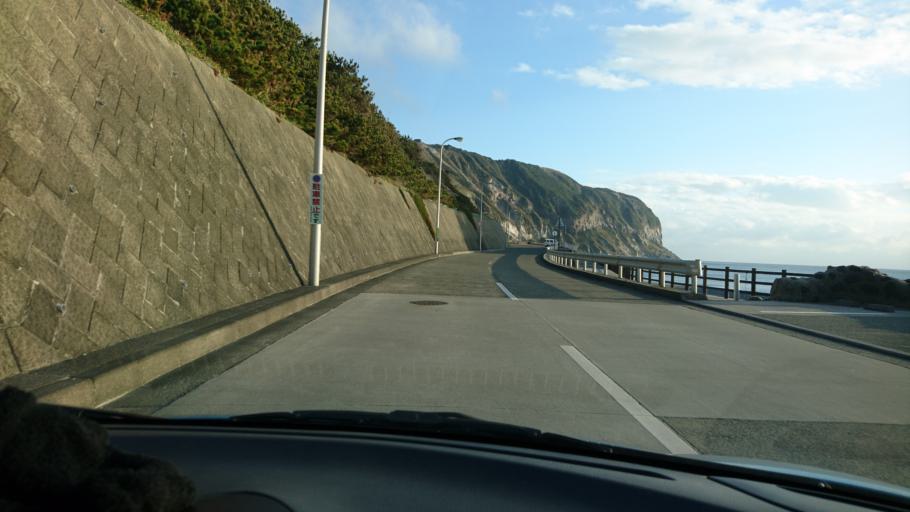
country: JP
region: Shizuoka
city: Shimoda
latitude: 34.3640
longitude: 139.2430
